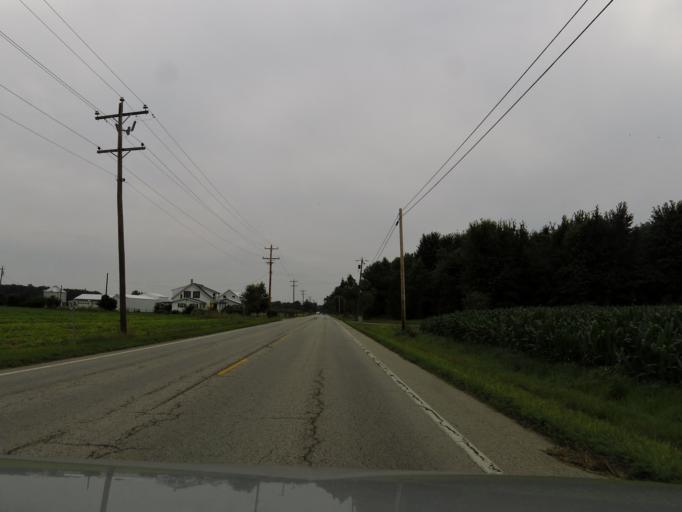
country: US
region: Ohio
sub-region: Brown County
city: Mount Orab
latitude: 39.0854
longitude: -83.9285
